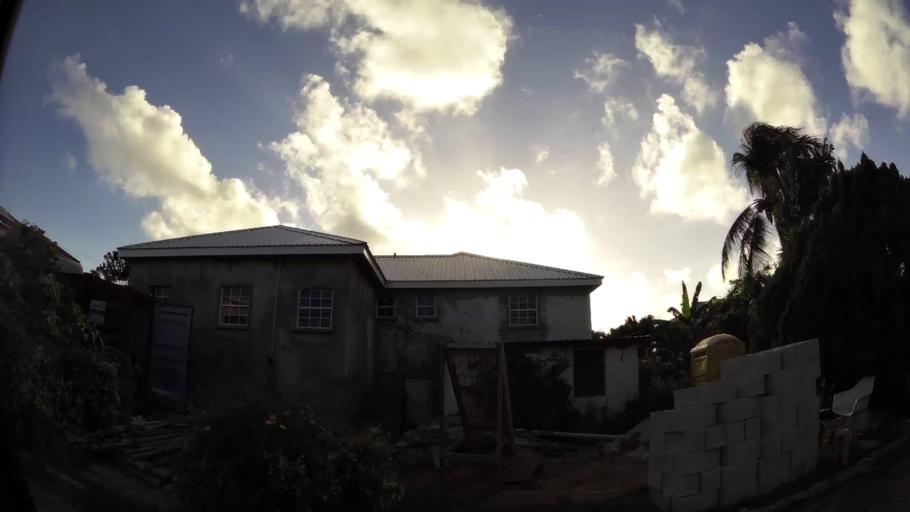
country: BB
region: Christ Church
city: Oistins
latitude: 13.0684
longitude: -59.5520
